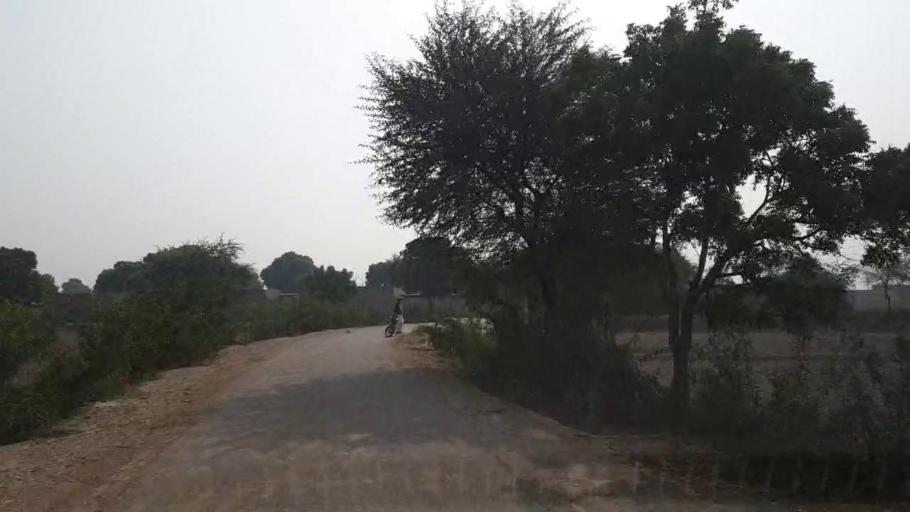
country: PK
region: Sindh
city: Tando Muhammad Khan
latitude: 25.1840
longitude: 68.6238
